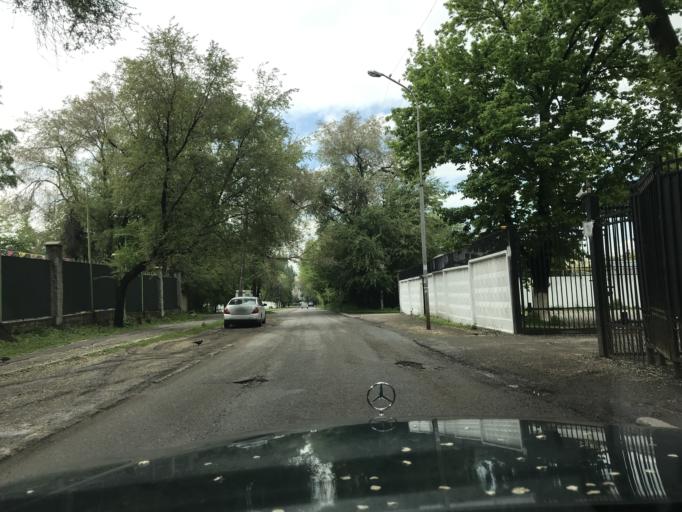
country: KZ
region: Almaty Qalasy
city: Almaty
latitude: 43.2067
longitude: 76.8708
